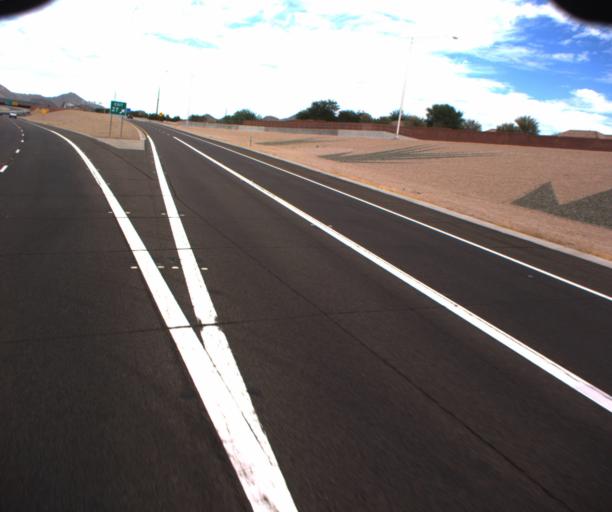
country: US
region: Arizona
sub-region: Pinal County
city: Apache Junction
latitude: 33.4175
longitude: -111.6359
